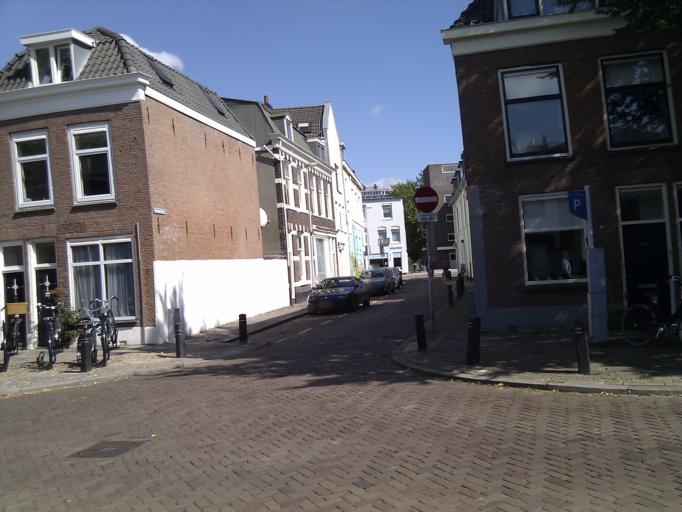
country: NL
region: Utrecht
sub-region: Gemeente Utrecht
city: Utrecht
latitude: 52.0960
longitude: 5.1068
